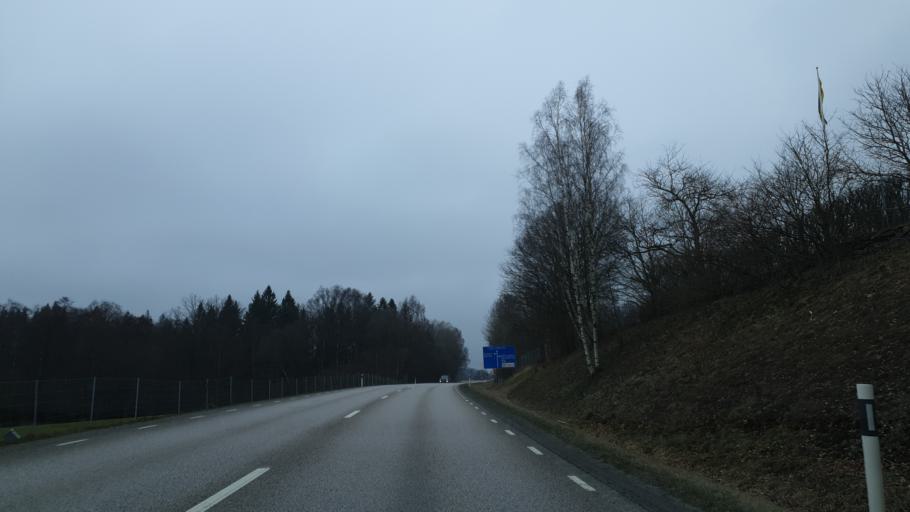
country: SE
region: Vaestra Goetaland
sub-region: Harryda Kommun
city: Ravlanda
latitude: 57.6153
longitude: 12.4347
